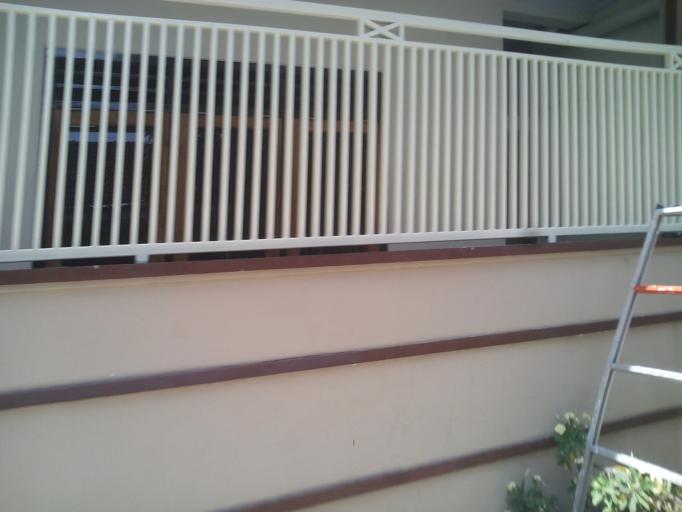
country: ID
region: East Java
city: Sumbersari Wetan
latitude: -8.1765
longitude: 113.7148
